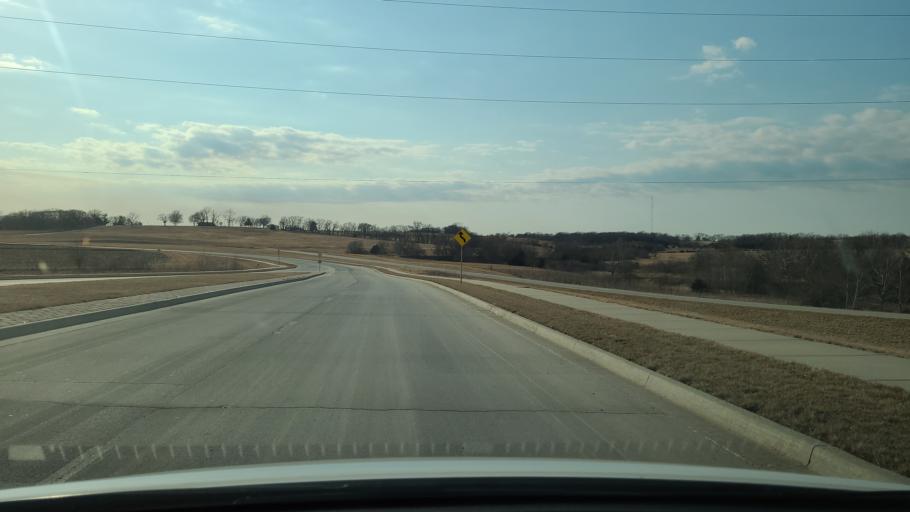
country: US
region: Kansas
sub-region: Douglas County
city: Lawrence
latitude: 38.9574
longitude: -95.3384
